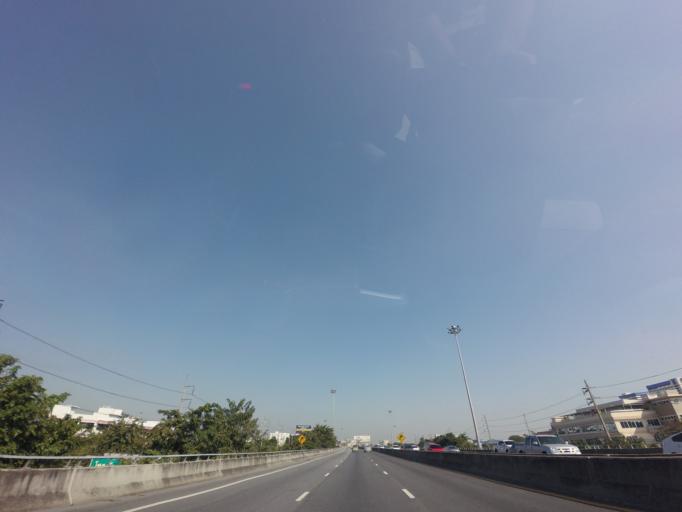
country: TH
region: Bangkok
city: Wang Thonglang
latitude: 13.7814
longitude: 100.6077
